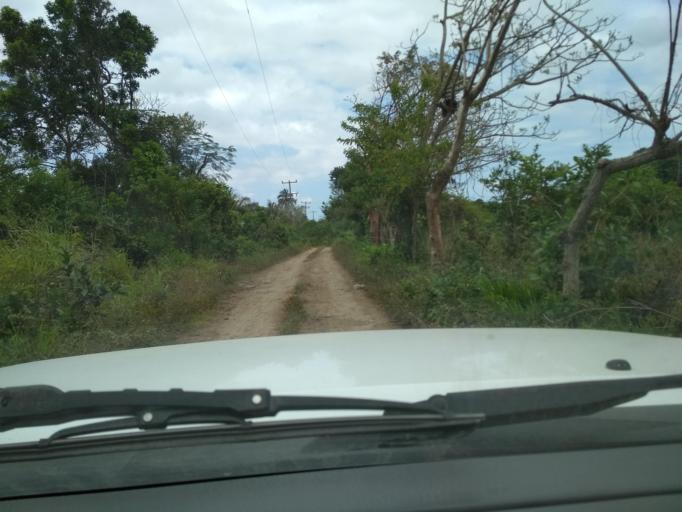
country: MX
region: Veracruz
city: El Tejar
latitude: 19.0590
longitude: -96.1463
